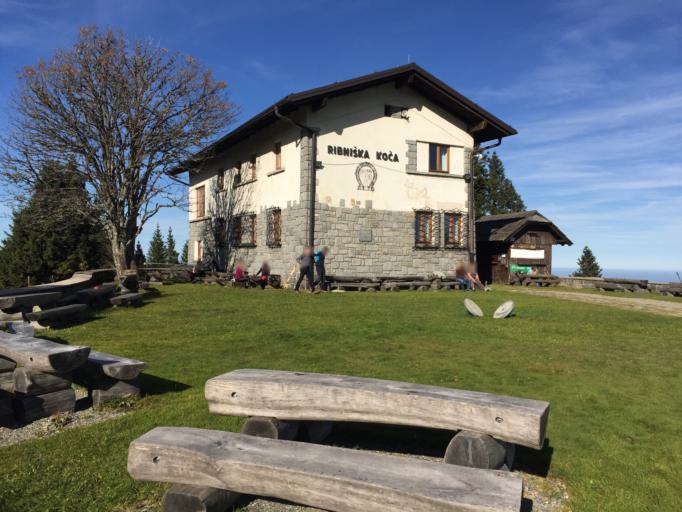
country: SI
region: Mislinja
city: Mislinja
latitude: 46.4976
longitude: 15.2555
